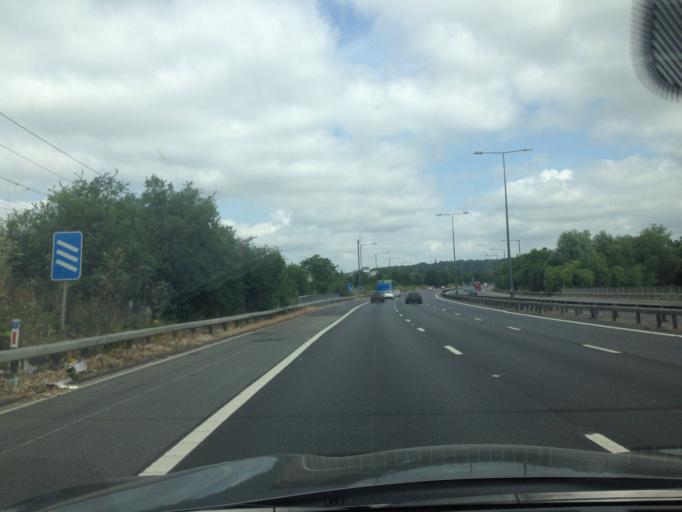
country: GB
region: England
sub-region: Greater London
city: Edgware
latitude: 51.6253
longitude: -0.2608
